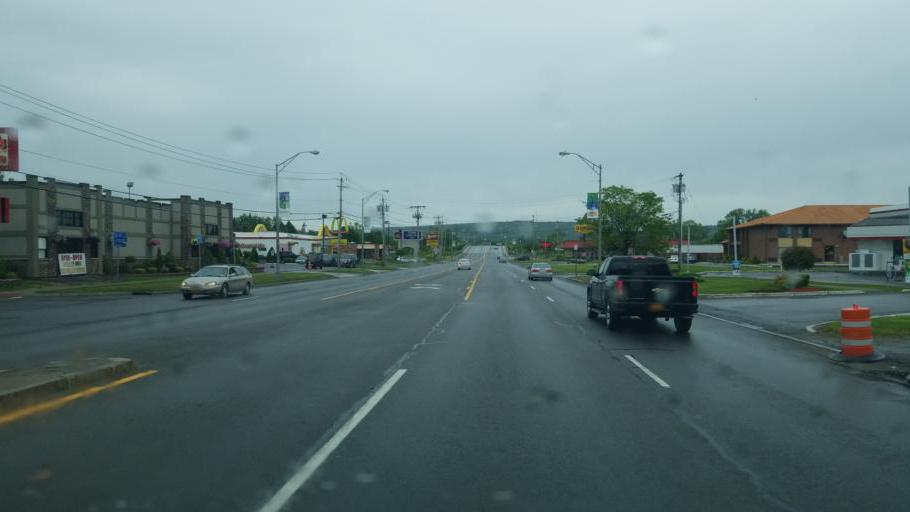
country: US
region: New York
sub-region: Oneida County
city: Utica
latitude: 43.1088
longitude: -75.2197
